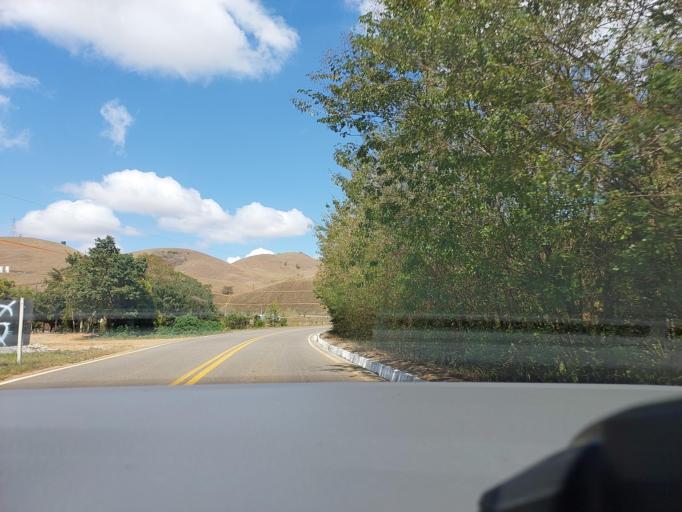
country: BR
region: Minas Gerais
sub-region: Muriae
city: Muriae
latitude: -21.0706
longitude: -42.5068
